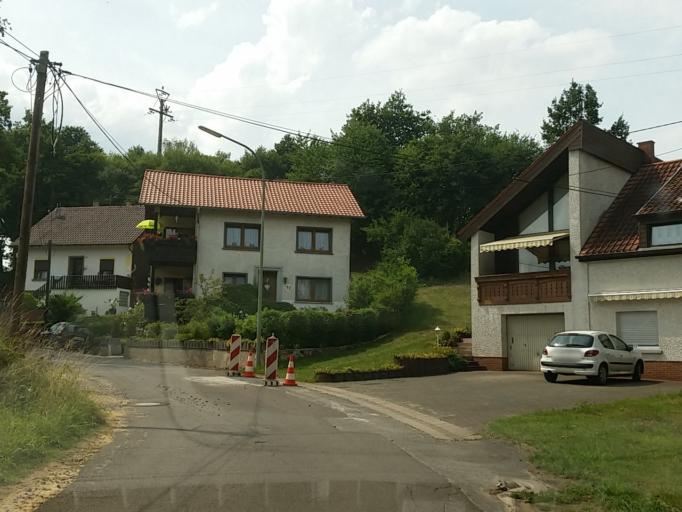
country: DE
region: Saarland
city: Schmelz
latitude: 49.4273
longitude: 6.8425
